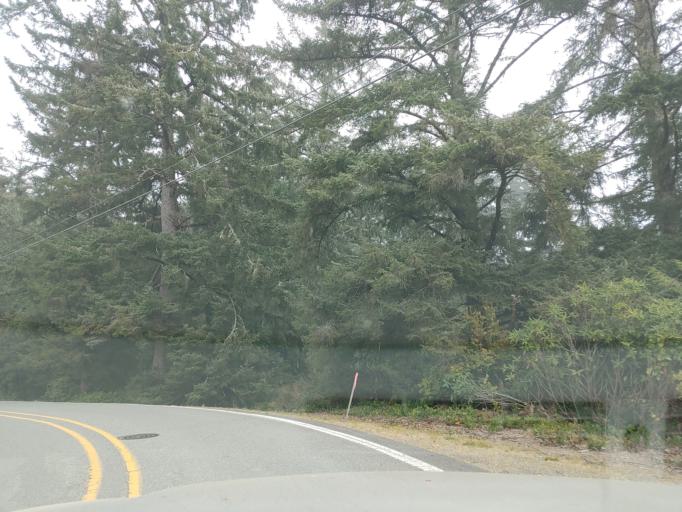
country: US
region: Oregon
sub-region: Coos County
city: Lakeside
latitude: 43.6632
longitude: -124.1981
